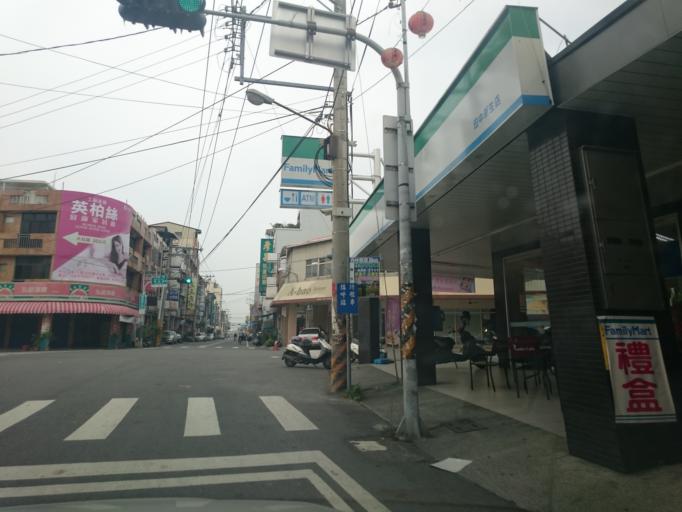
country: TW
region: Taiwan
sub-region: Nantou
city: Nantou
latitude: 23.8626
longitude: 120.5850
